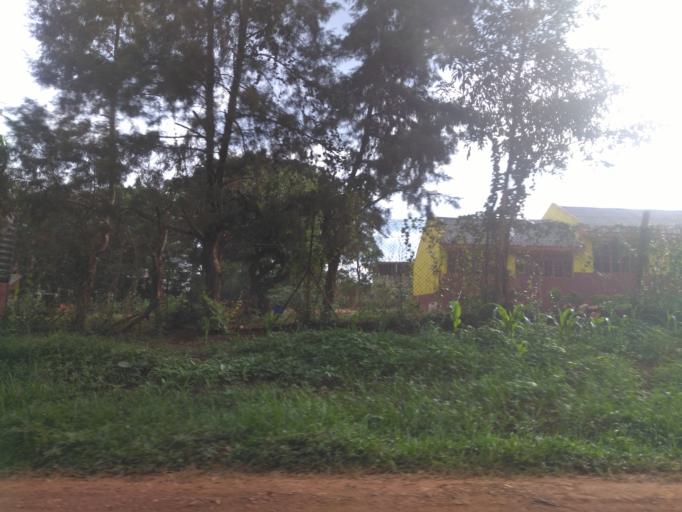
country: UG
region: Eastern Region
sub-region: Jinja District
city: Jinja
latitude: 0.4221
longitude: 33.2116
